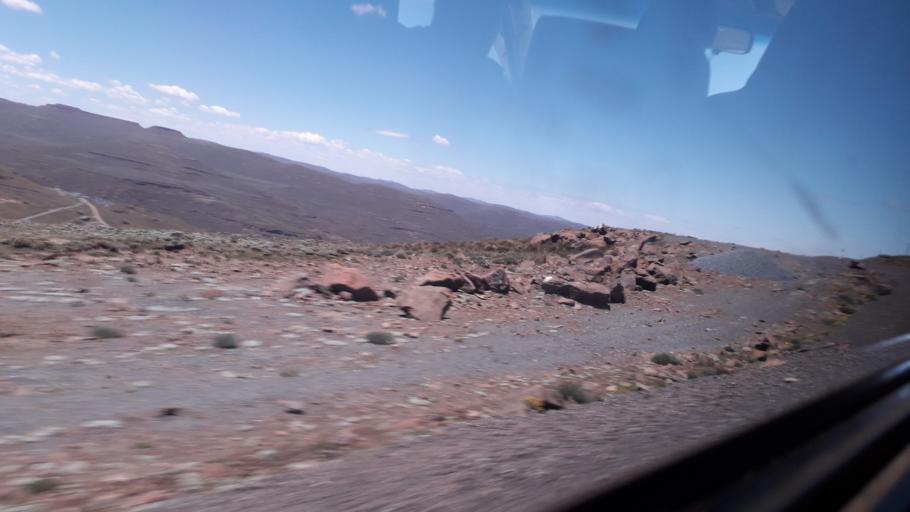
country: ZA
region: Orange Free State
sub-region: Thabo Mofutsanyana District Municipality
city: Phuthaditjhaba
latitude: -28.8094
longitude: 28.7258
